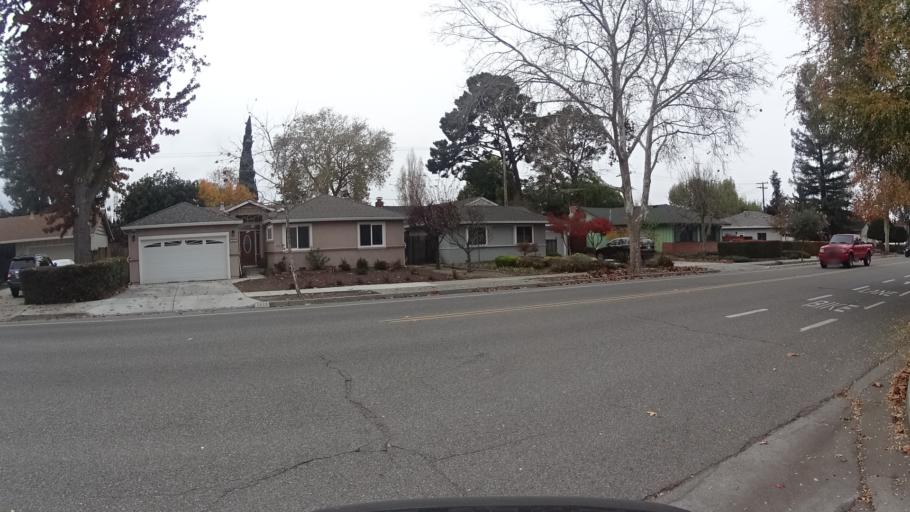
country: US
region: California
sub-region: Santa Clara County
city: Sunnyvale
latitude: 37.3630
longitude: -122.0593
